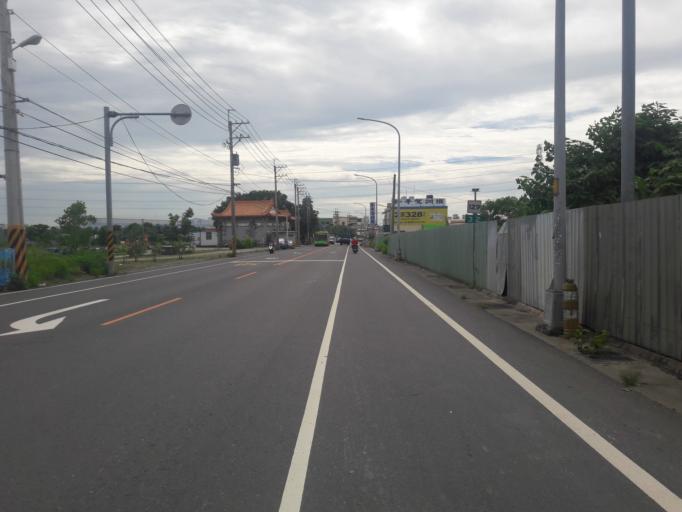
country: TW
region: Taiwan
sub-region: Taichung City
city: Taichung
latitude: 24.0942
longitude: 120.7110
